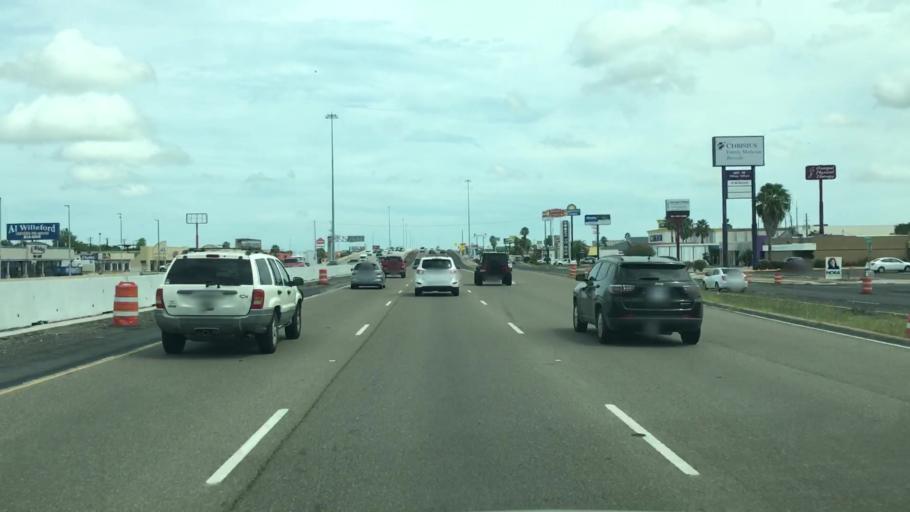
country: US
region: Texas
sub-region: Nueces County
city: Corpus Christi
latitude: 27.7236
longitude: -97.4029
